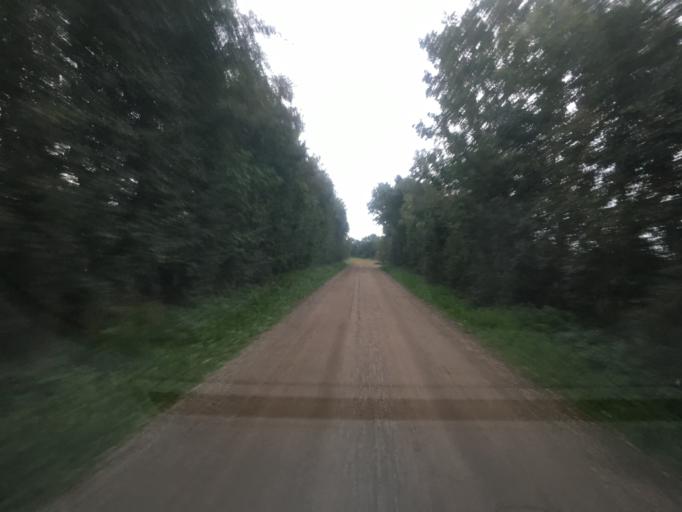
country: DK
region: South Denmark
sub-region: Tonder Kommune
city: Logumkloster
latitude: 54.9743
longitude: 9.0291
